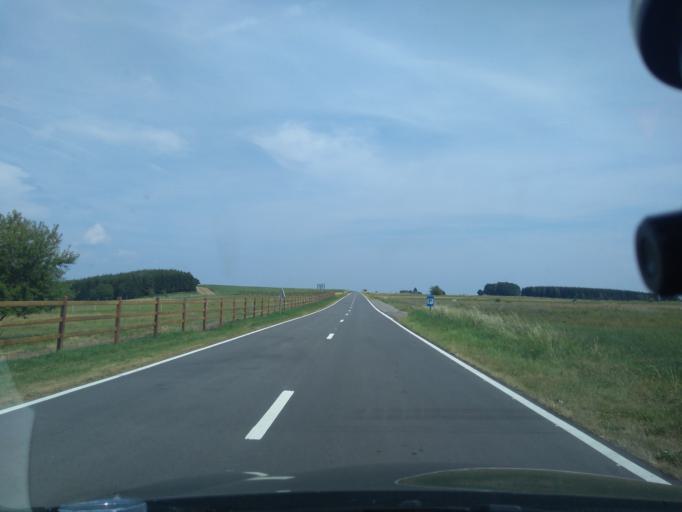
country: BE
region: Wallonia
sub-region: Province du Luxembourg
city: Bertogne
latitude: 50.1493
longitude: 5.6975
